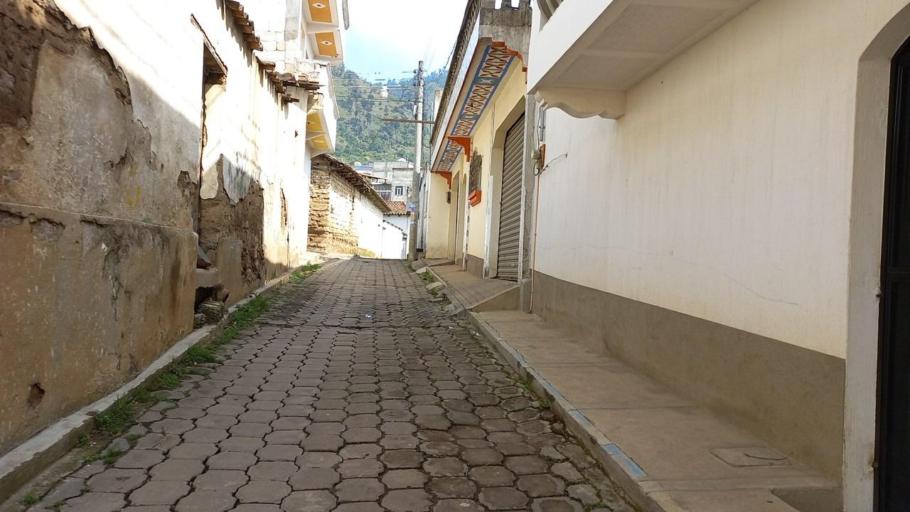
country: GT
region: Totonicapan
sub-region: Municipio de San Andres Xecul
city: San Andres Xecul
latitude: 14.9030
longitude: -91.4836
